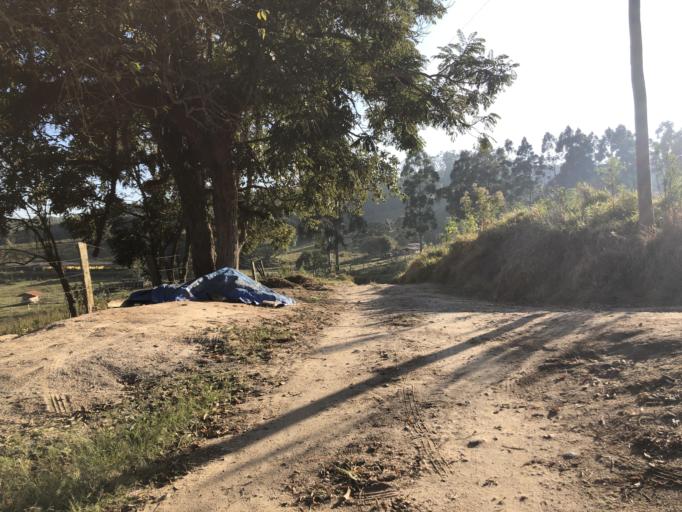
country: BR
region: Sao Paulo
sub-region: Pilar Do Sul
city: Pilar do Sul
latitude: -23.8293
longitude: -47.6257
